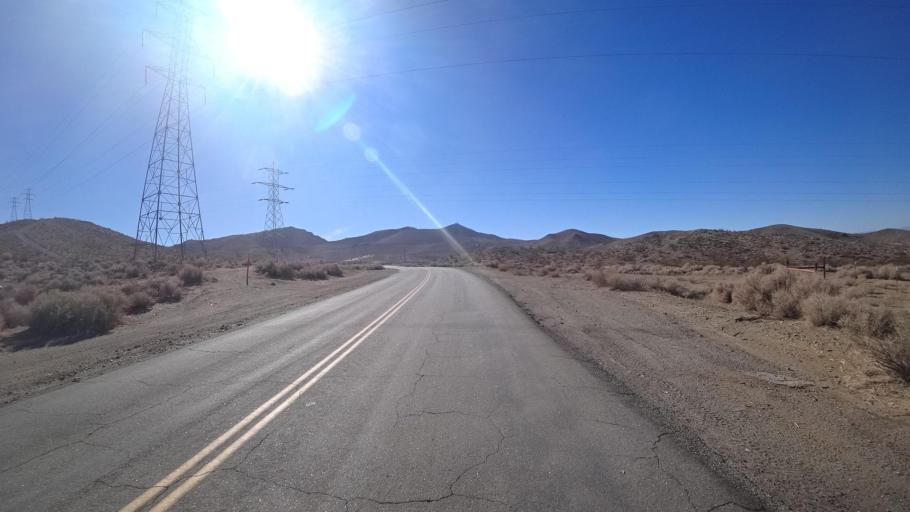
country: US
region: California
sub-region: Kern County
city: Ridgecrest
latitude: 35.3760
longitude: -117.6551
